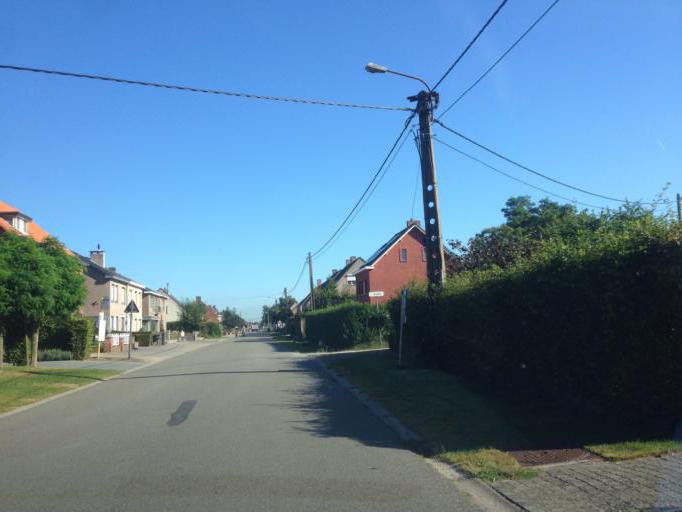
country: BE
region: Flanders
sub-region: Provincie Antwerpen
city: Geel
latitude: 51.1750
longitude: 4.9946
